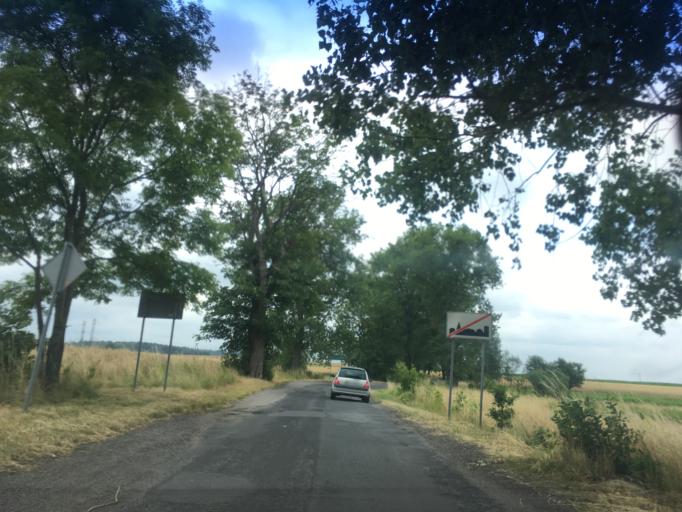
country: PL
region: Lower Silesian Voivodeship
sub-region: Powiat zgorzelecki
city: Sulikow
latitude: 51.1008
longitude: 15.0651
